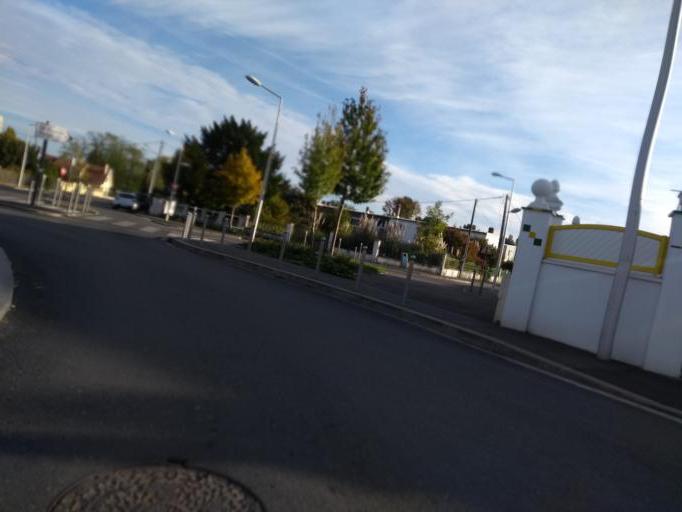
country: FR
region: Aquitaine
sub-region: Departement de la Gironde
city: Pessac
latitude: 44.7928
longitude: -0.6423
